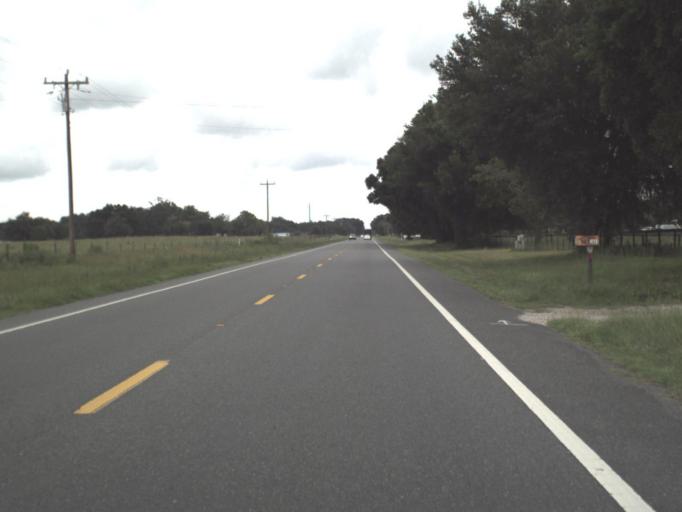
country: US
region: Florida
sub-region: Levy County
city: Williston
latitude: 29.3085
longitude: -82.4502
